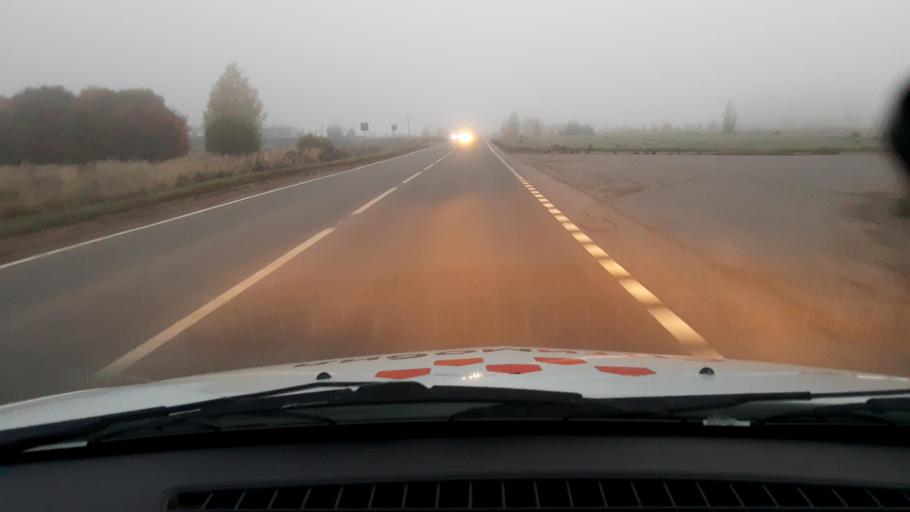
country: RU
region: Bashkortostan
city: Kabakovo
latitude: 54.7369
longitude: 56.2034
